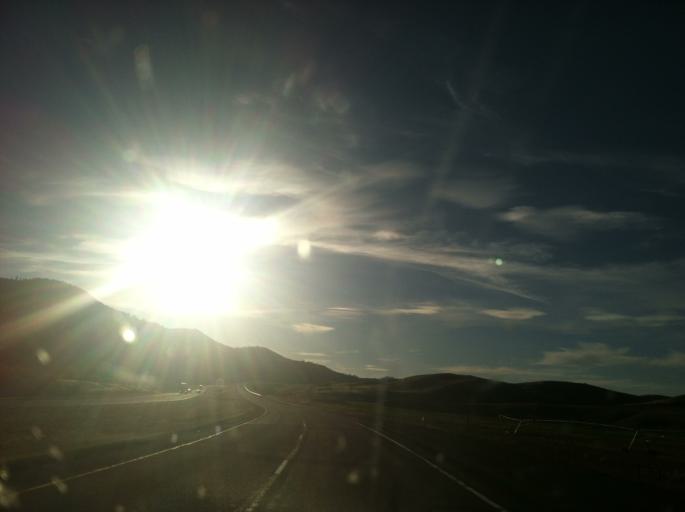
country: US
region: Montana
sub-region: Granite County
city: Philipsburg
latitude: 46.6975
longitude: -113.2118
